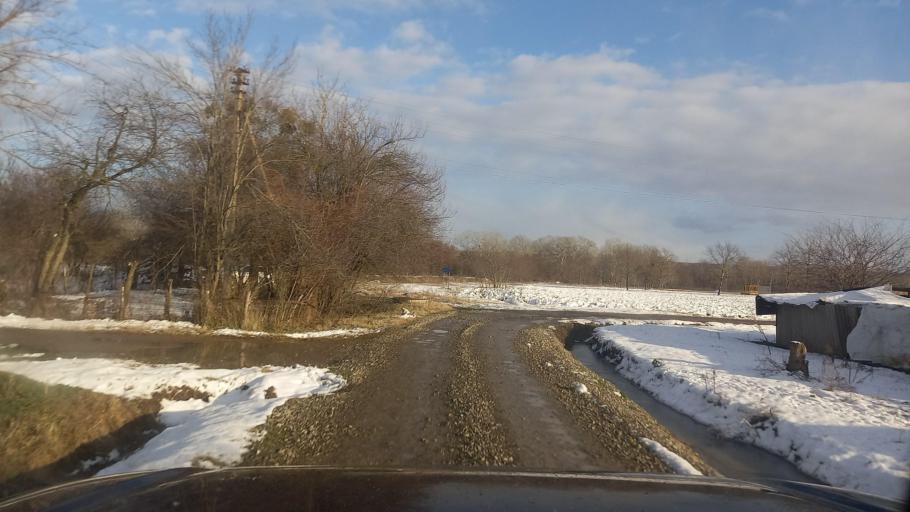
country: RU
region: Krasnodarskiy
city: Smolenskaya
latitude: 44.7760
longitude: 38.8500
